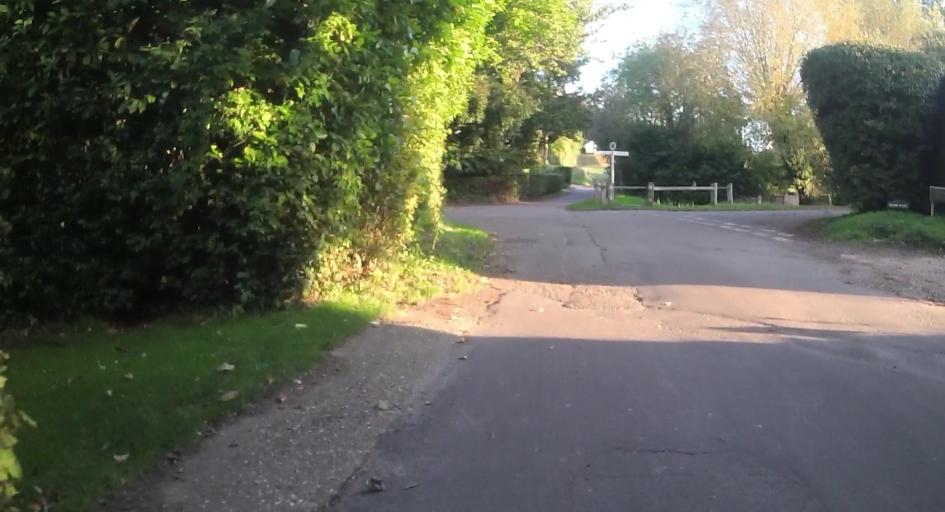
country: GB
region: England
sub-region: Hampshire
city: Old Basing
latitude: 51.2567
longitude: -1.0160
